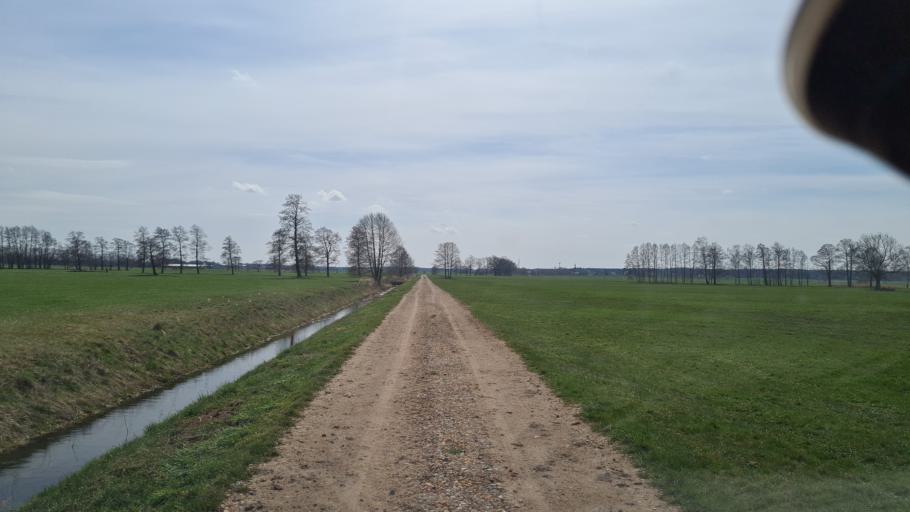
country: DE
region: Brandenburg
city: Bronkow
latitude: 51.6087
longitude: 13.9267
